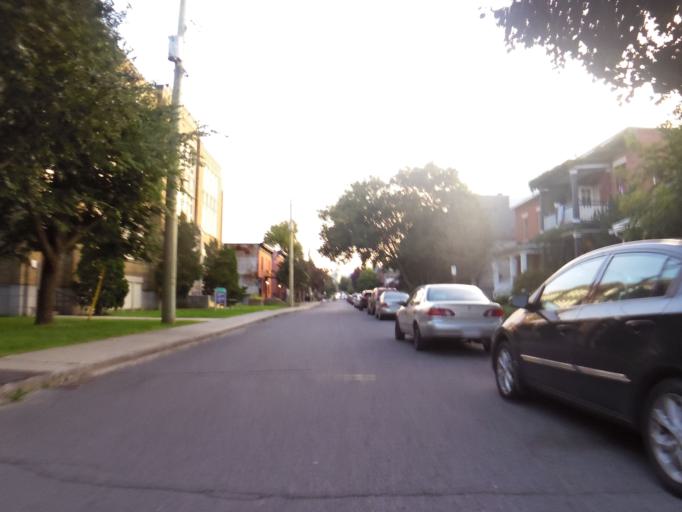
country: CA
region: Ontario
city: Ottawa
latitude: 45.4324
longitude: -75.6915
